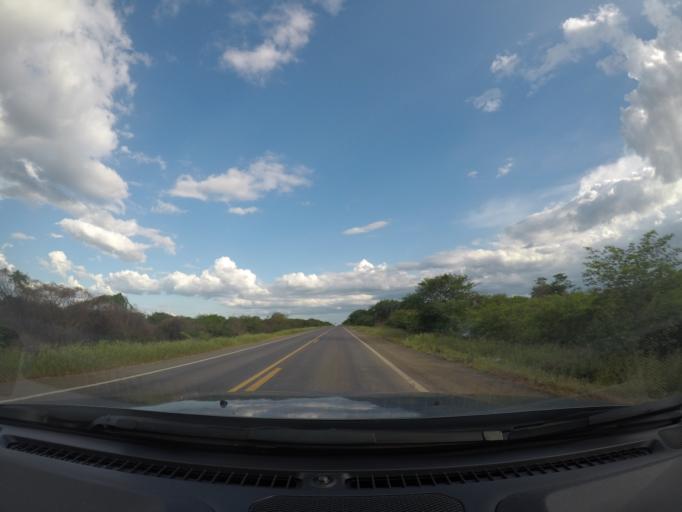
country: BR
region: Bahia
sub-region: Oliveira Dos Brejinhos
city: Beira Rio
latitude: -12.1896
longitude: -42.8248
